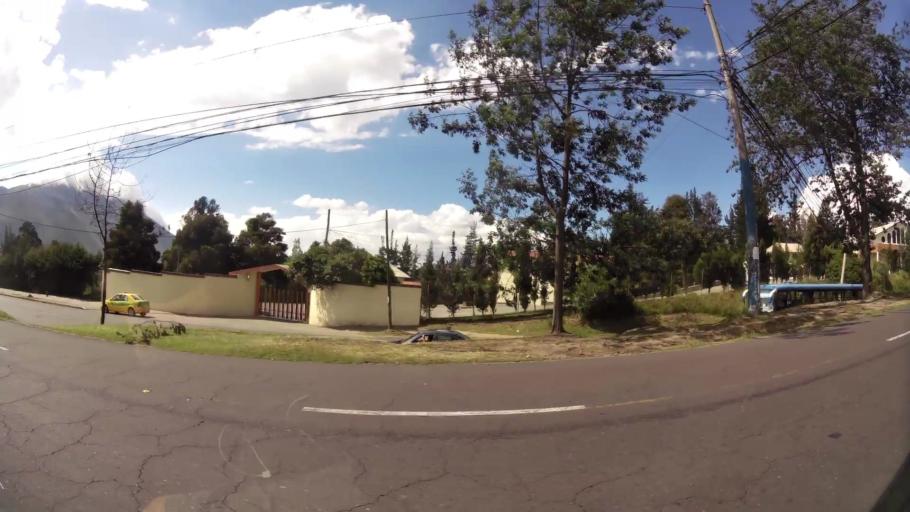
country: EC
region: Pichincha
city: Quito
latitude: -0.0952
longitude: -78.4697
